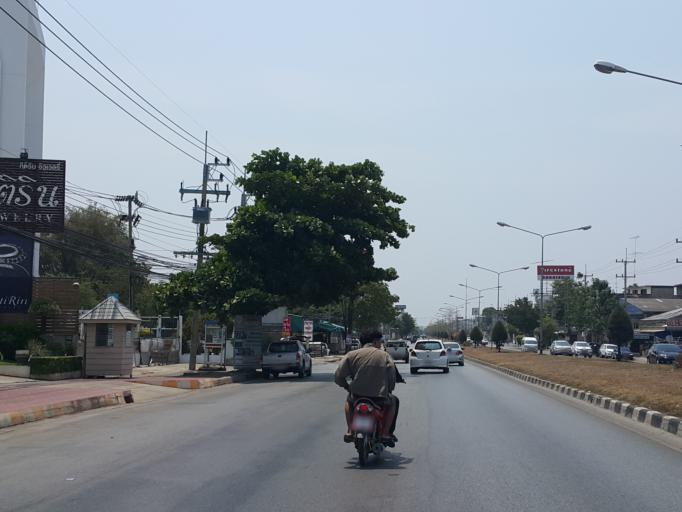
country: TH
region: Kanchanaburi
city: Kanchanaburi
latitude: 14.0454
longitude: 99.5106
